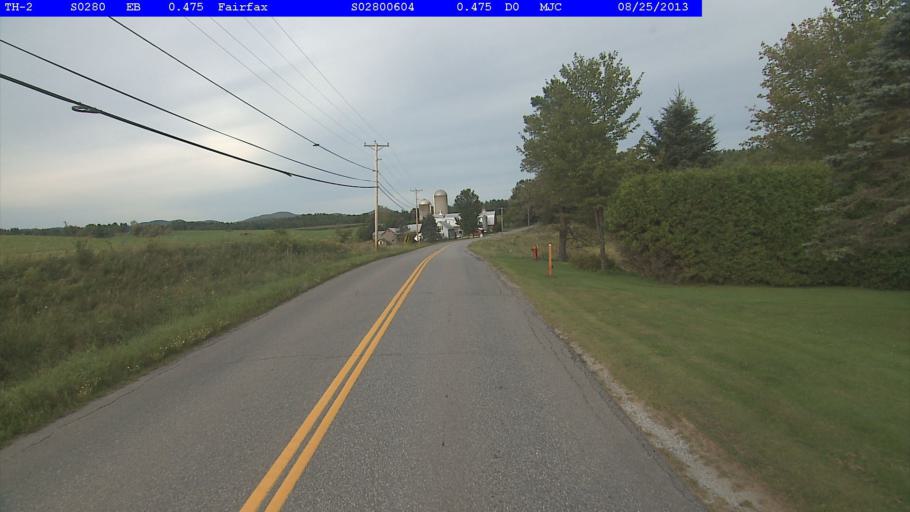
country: US
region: Vermont
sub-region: Chittenden County
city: Milton
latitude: 44.6687
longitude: -73.0022
